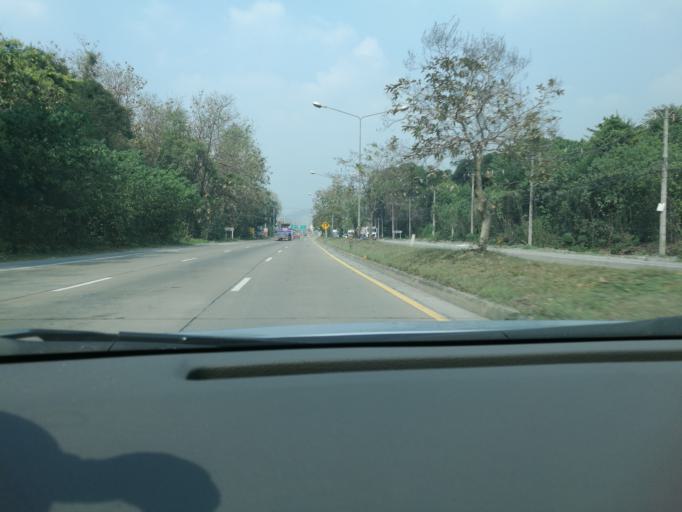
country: TH
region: Sara Buri
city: Chaloem Phra Kiat
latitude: 14.6824
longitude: 100.8742
